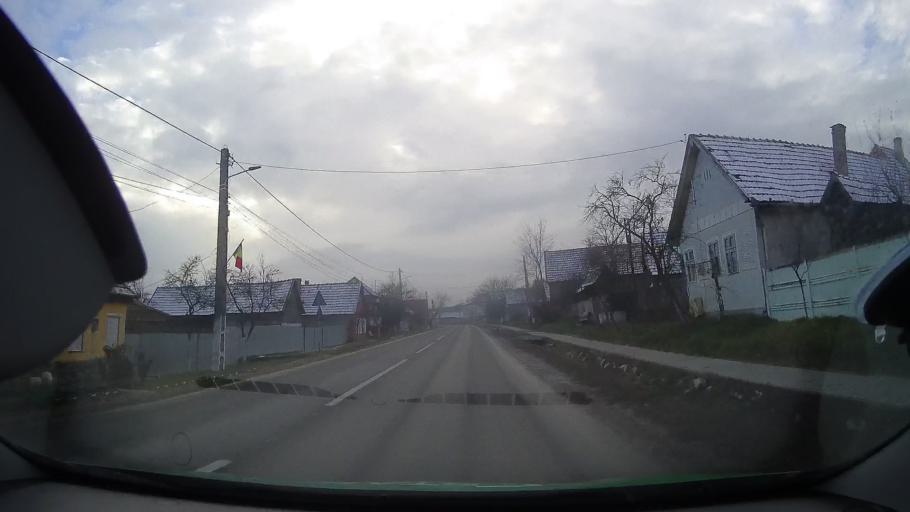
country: RO
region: Mures
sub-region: Comuna Cucerdea
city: Cucerdea
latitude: 46.4027
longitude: 24.2627
